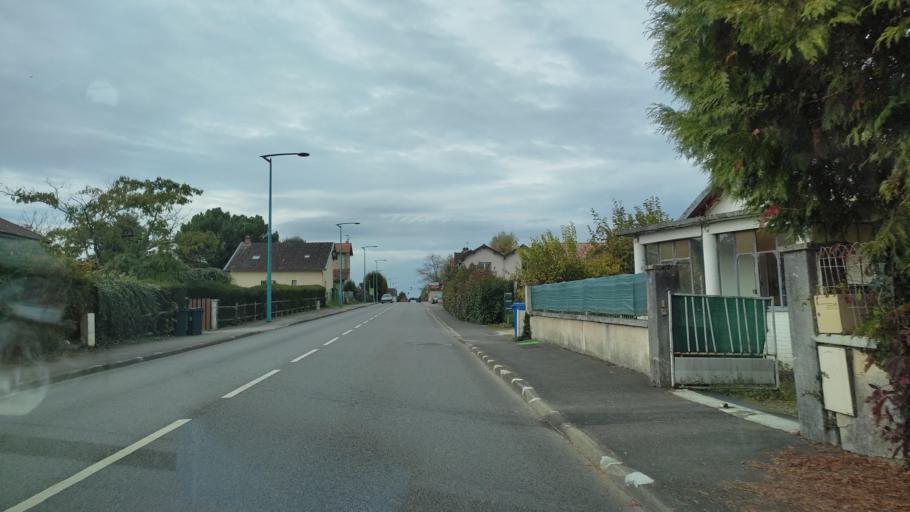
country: FR
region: Limousin
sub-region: Departement de la Haute-Vienne
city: Rilhac-Rancon
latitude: 45.9024
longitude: 1.3198
